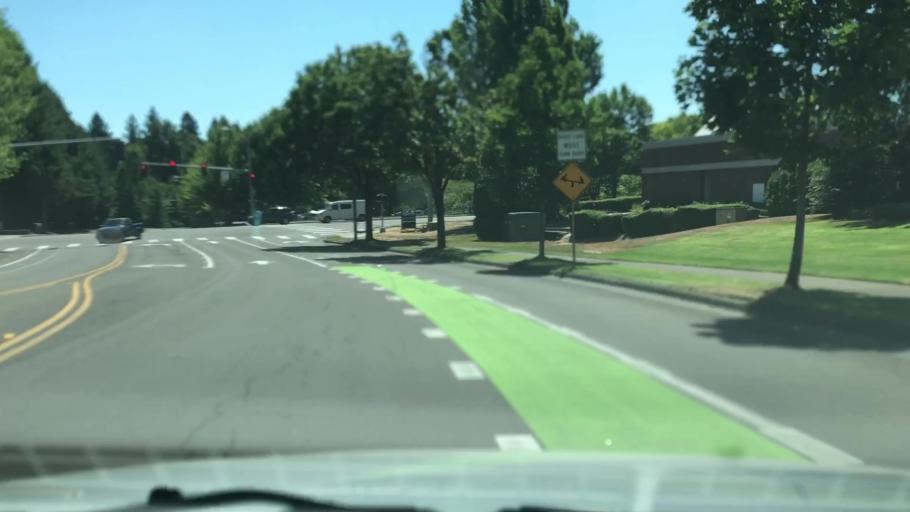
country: US
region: Oregon
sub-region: Clackamas County
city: Wilsonville
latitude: 45.3036
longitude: -122.7603
